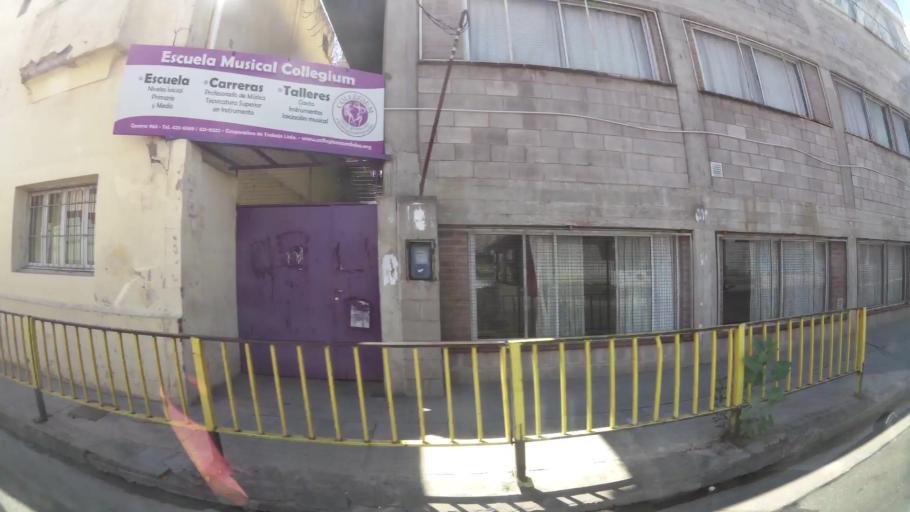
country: AR
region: Cordoba
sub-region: Departamento de Capital
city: Cordoba
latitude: -31.4149
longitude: -64.1985
